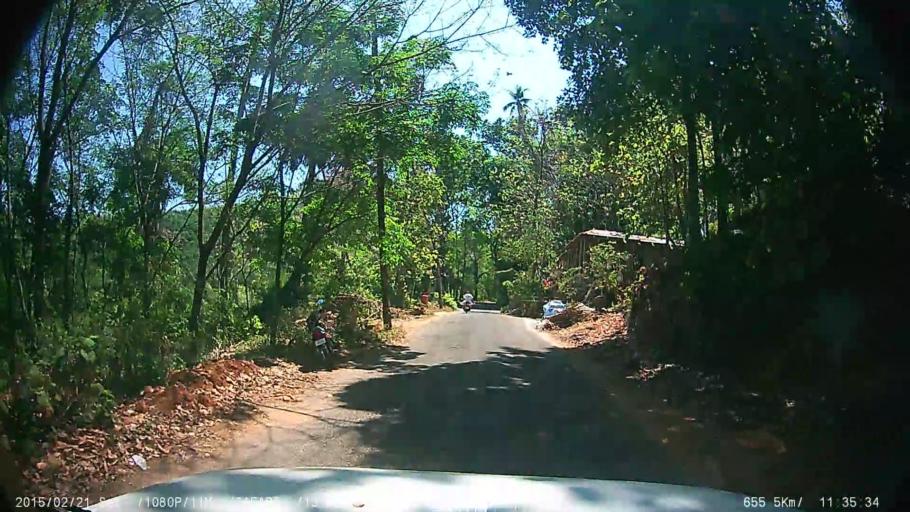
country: IN
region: Kerala
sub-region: Kottayam
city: Lalam
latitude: 9.8172
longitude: 76.7231
